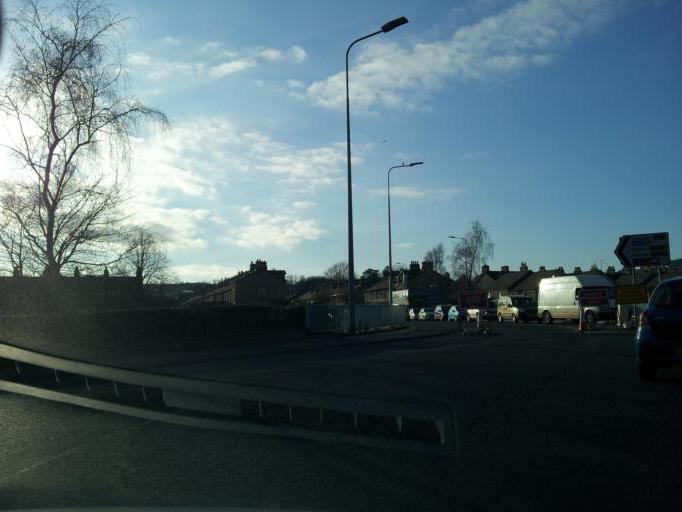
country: GB
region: England
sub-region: Cumbria
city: Kendal
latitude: 54.3167
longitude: -2.7418
